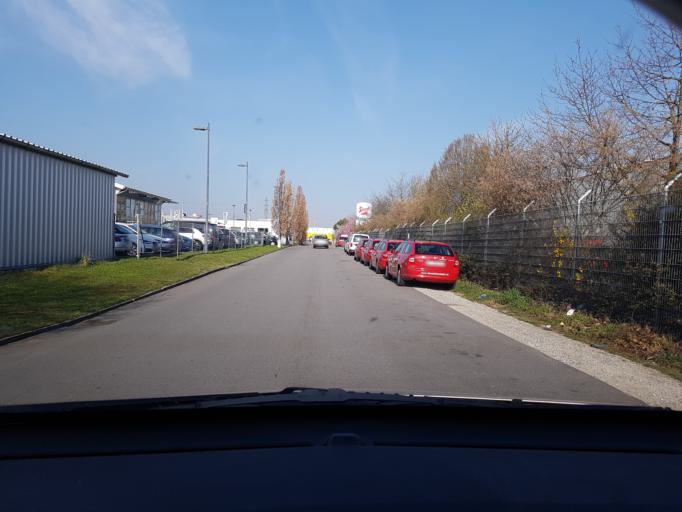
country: AT
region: Upper Austria
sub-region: Politischer Bezirk Linz-Land
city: Asten
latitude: 48.2233
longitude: 14.4080
